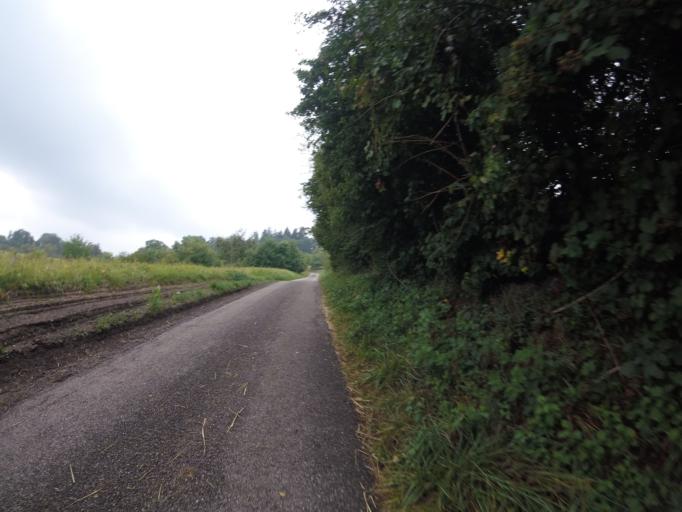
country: DE
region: Baden-Wuerttemberg
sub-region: Regierungsbezirk Stuttgart
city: Oppenweiler
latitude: 48.9828
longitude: 9.4445
